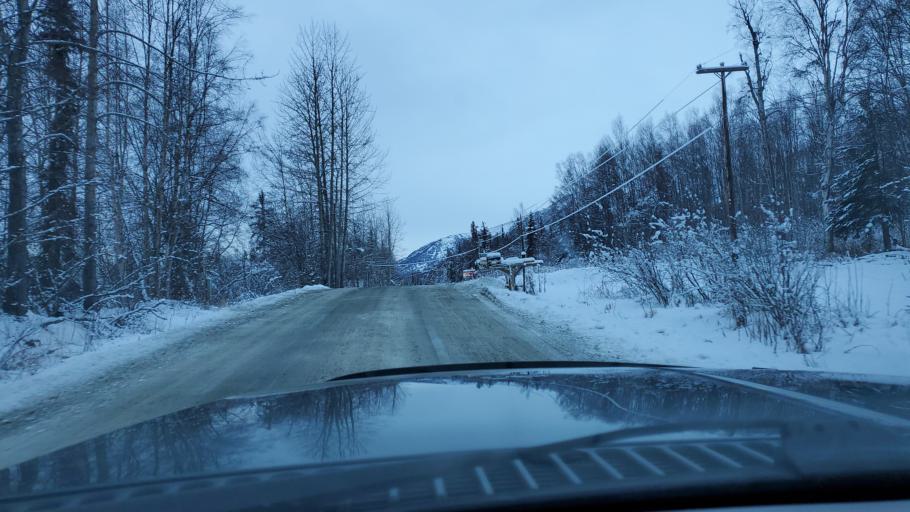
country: US
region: Alaska
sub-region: Matanuska-Susitna Borough
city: Lakes
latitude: 61.6933
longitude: -149.3123
